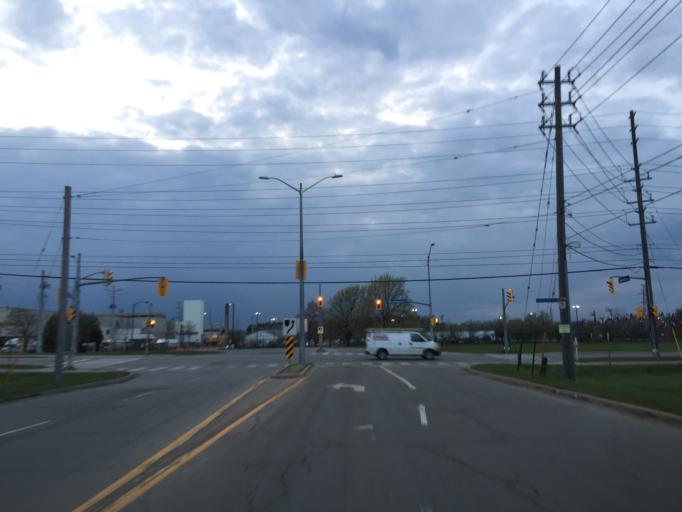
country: CA
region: Ontario
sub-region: Wellington County
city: Guelph
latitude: 43.5565
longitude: -80.2888
